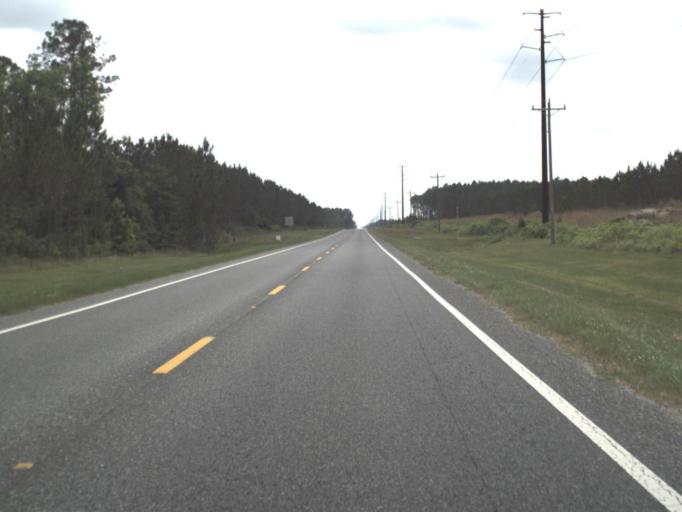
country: US
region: Florida
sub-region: Clay County
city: Middleburg
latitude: 30.0095
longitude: -81.8977
